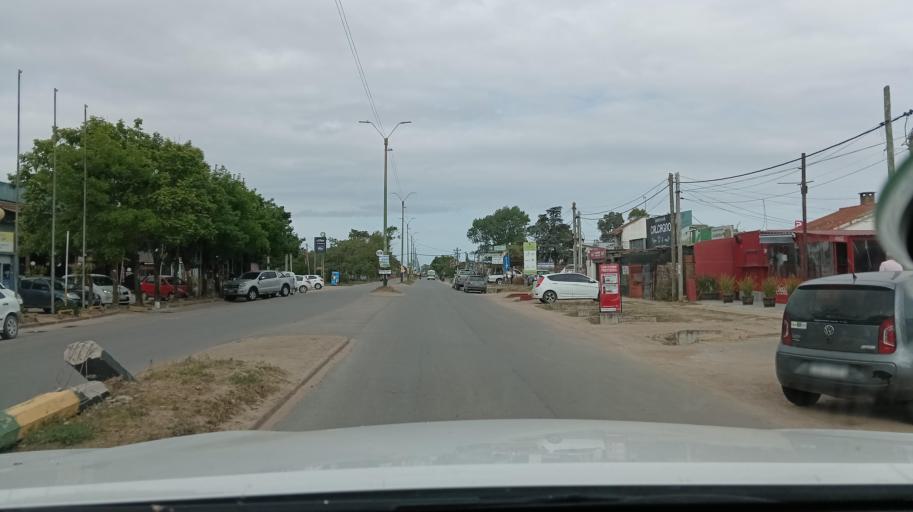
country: UY
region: Canelones
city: Barra de Carrasco
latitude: -34.8500
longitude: -55.9995
